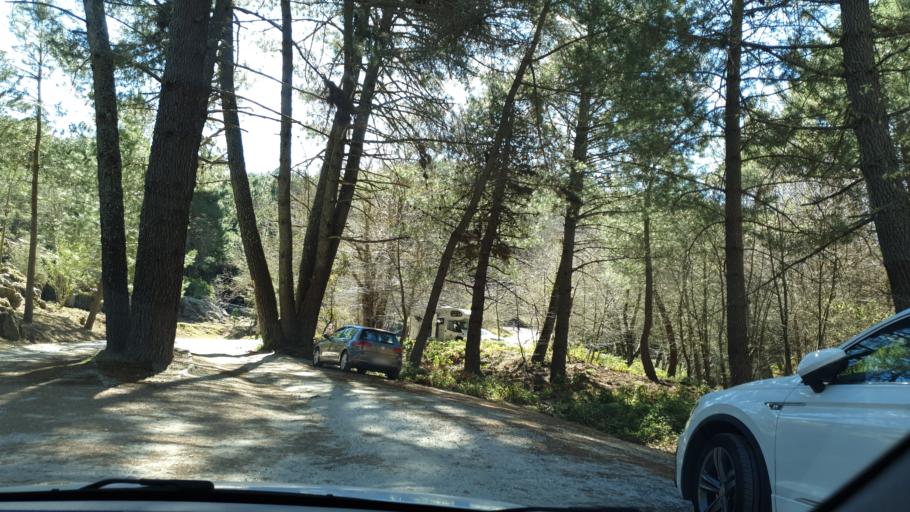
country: ES
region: Andalusia
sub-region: Provincia de Malaga
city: Ojen
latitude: 36.5788
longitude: -4.8845
